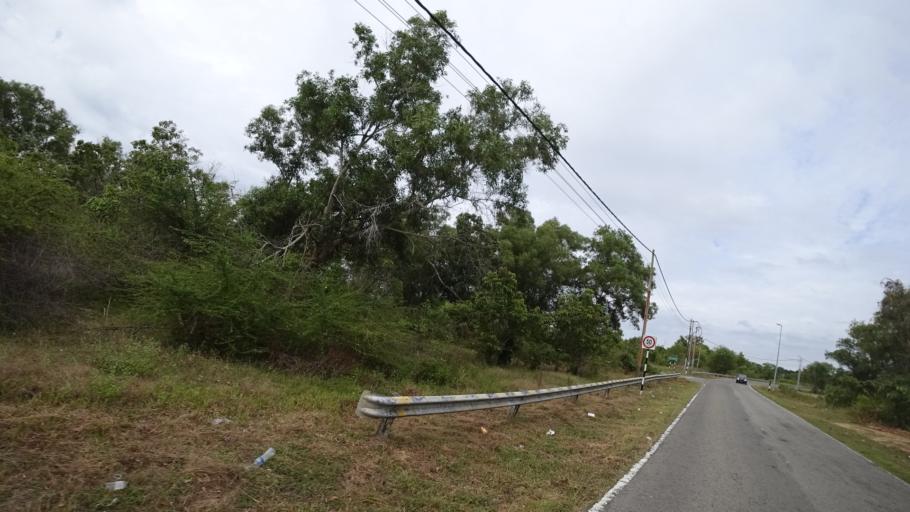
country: BN
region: Tutong
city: Tutong
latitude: 4.8074
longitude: 114.6395
